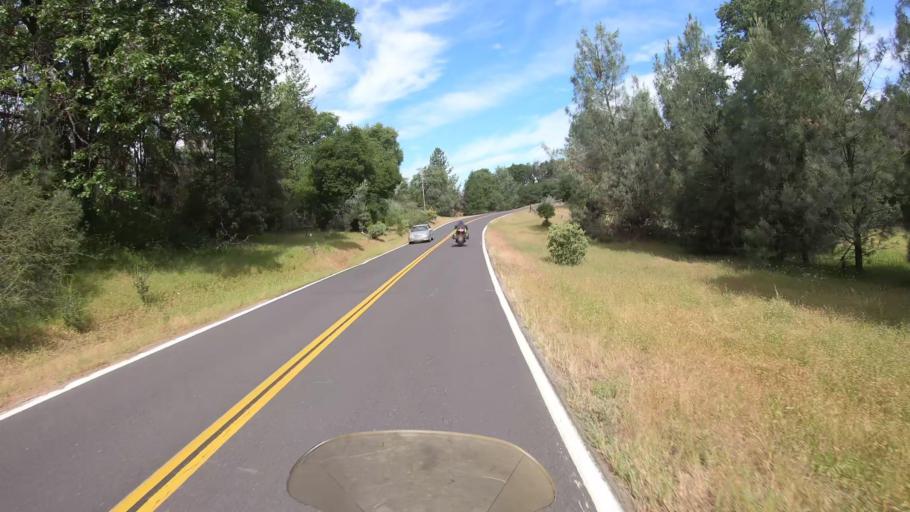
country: US
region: California
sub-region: Tuolumne County
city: Tuolumne City
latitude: 37.8520
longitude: -120.1674
